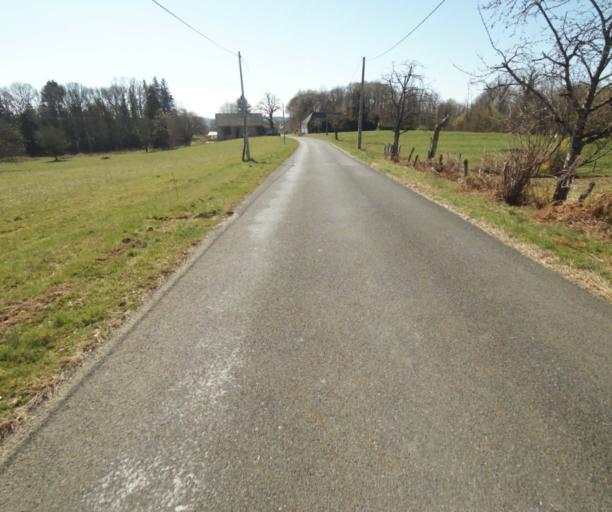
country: FR
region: Limousin
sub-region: Departement de la Correze
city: Saint-Mexant
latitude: 45.3203
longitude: 1.6466
